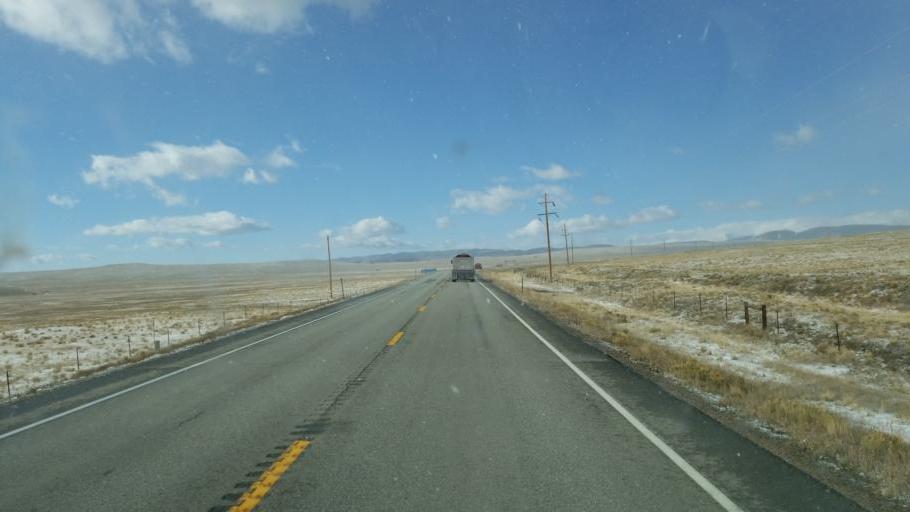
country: US
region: Colorado
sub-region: Park County
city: Fairplay
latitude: 39.3592
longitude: -105.8177
